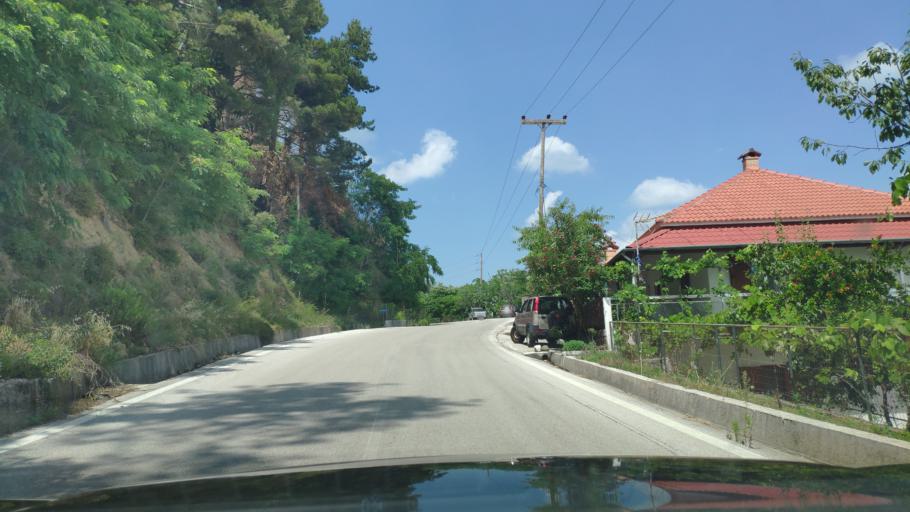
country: GR
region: Epirus
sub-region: Nomos Artas
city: Agios Dimitrios
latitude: 39.3227
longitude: 20.9947
